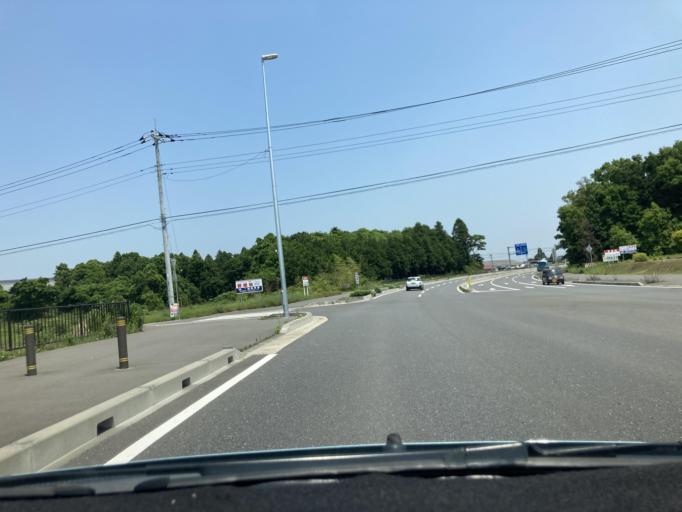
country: JP
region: Ibaraki
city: Ishige
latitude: 36.0817
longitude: 140.0633
